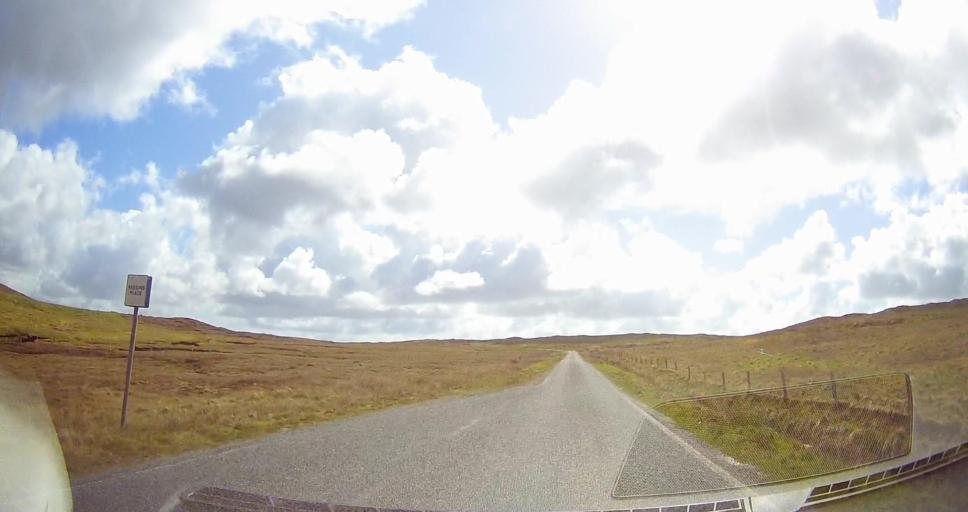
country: GB
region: Scotland
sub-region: Shetland Islands
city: Lerwick
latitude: 60.5031
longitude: -1.3937
